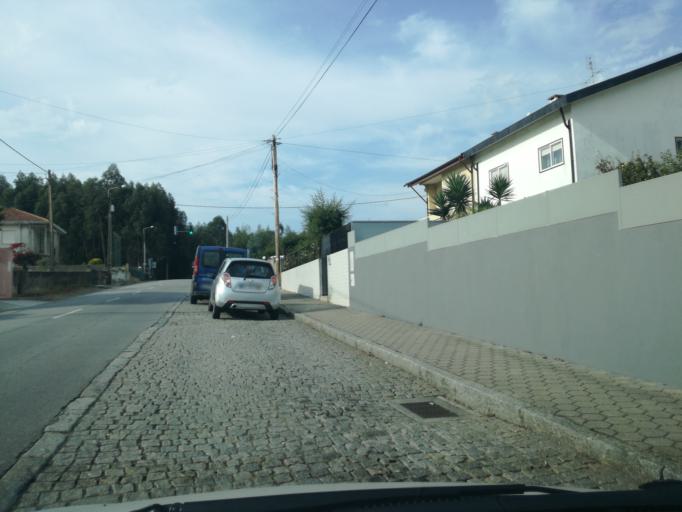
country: PT
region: Porto
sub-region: Vila Nova de Gaia
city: Sao Felix da Marinha
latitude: 41.0261
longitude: -8.6301
